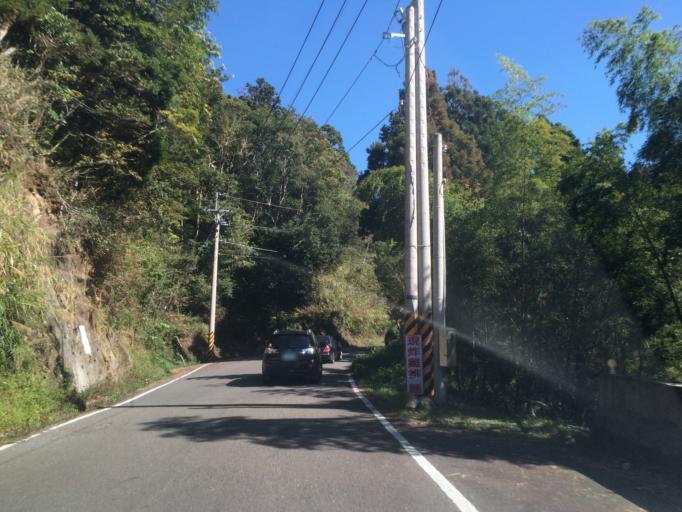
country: TW
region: Taiwan
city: Lugu
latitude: 23.6550
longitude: 120.7852
